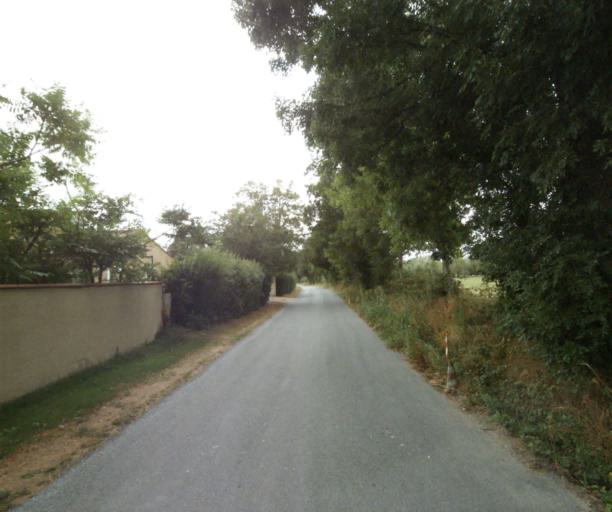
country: FR
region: Midi-Pyrenees
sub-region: Departement du Tarn
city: Soreze
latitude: 43.4558
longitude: 2.0631
